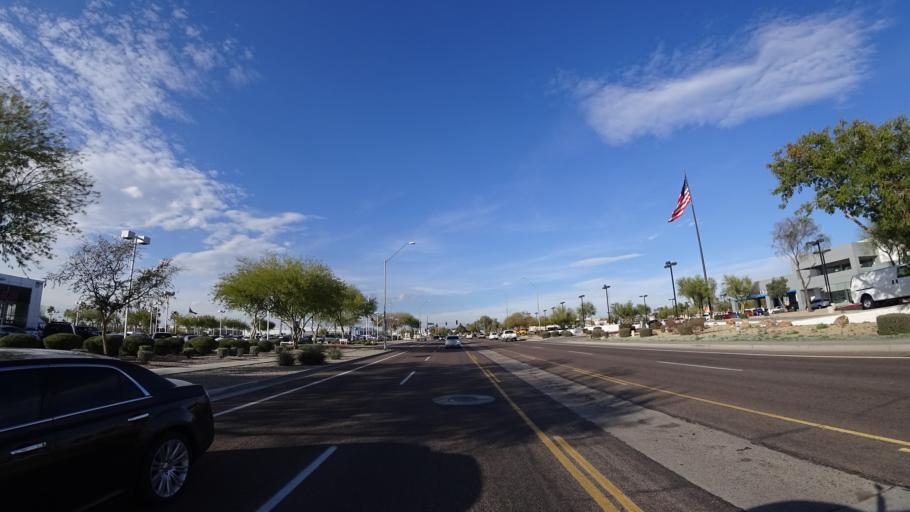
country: US
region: Arizona
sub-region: Maricopa County
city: Sun City
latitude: 33.6367
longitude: -112.2529
